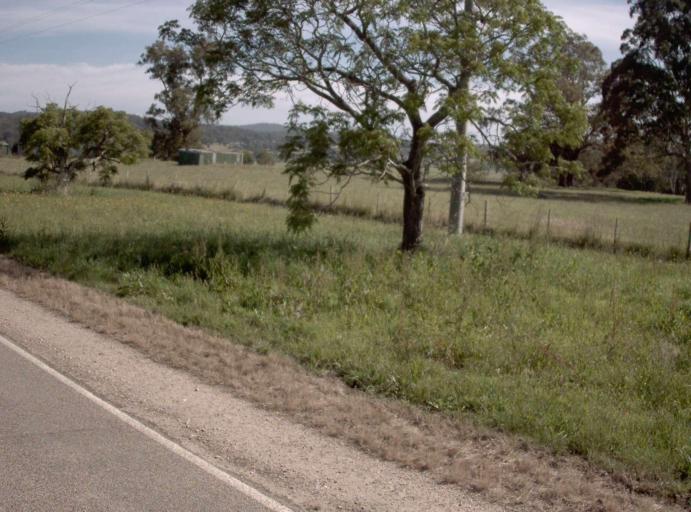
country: AU
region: Victoria
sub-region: East Gippsland
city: Bairnsdale
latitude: -37.7271
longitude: 147.8083
